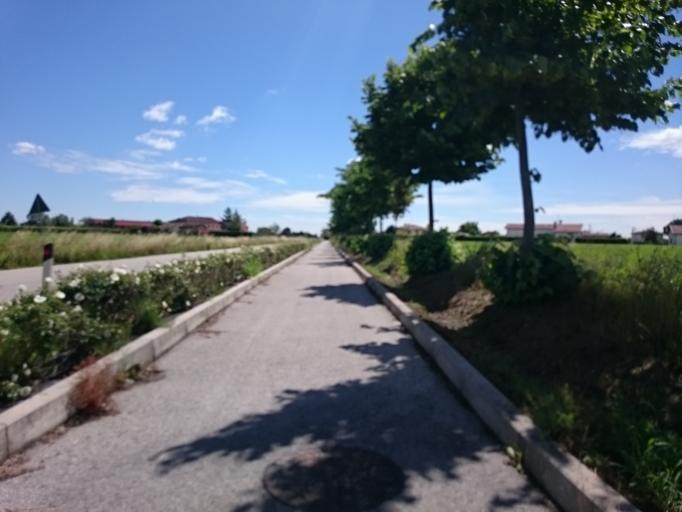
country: IT
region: Veneto
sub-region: Provincia di Padova
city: Polverara
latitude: 45.3193
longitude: 11.9506
